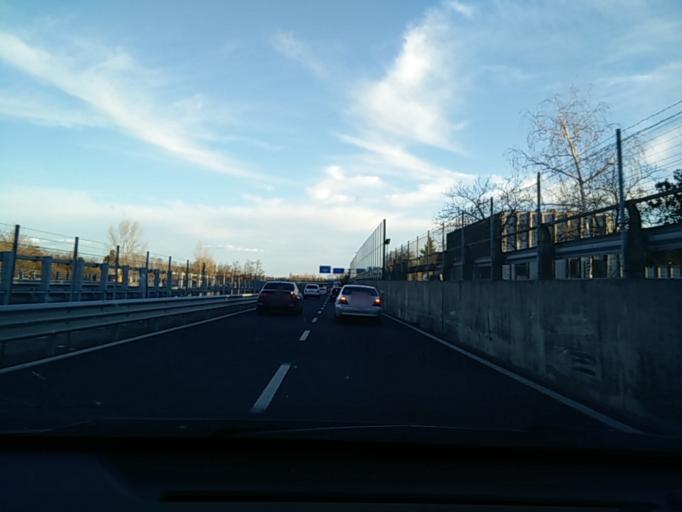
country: IT
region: Friuli Venezia Giulia
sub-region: Provincia di Udine
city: Pasian di Prato
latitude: 46.0535
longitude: 13.2021
